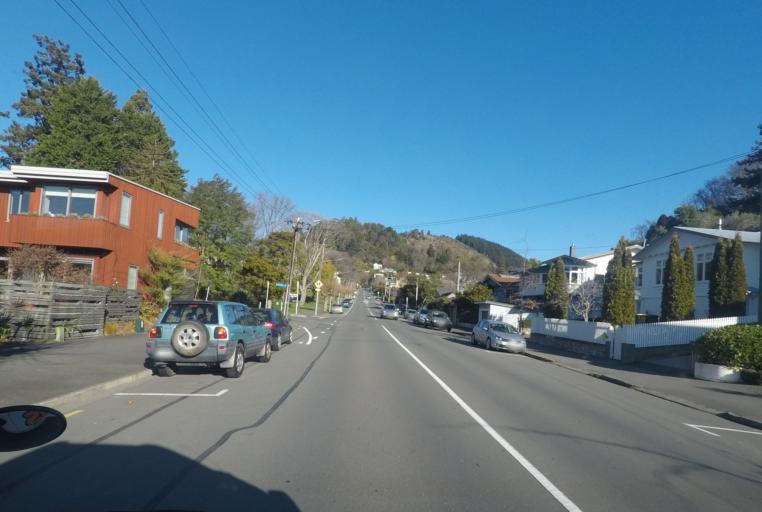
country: NZ
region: Nelson
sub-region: Nelson City
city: Nelson
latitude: -41.2778
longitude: 173.2868
